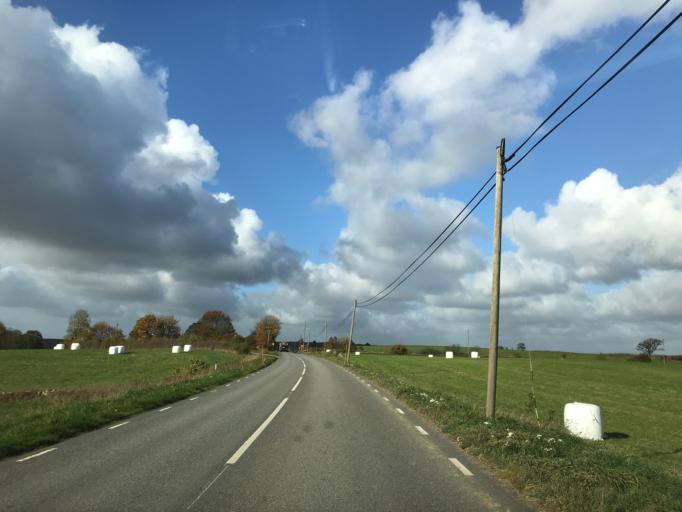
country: SE
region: Skane
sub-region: Perstorps Kommun
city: Perstorp
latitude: 56.0420
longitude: 13.3873
